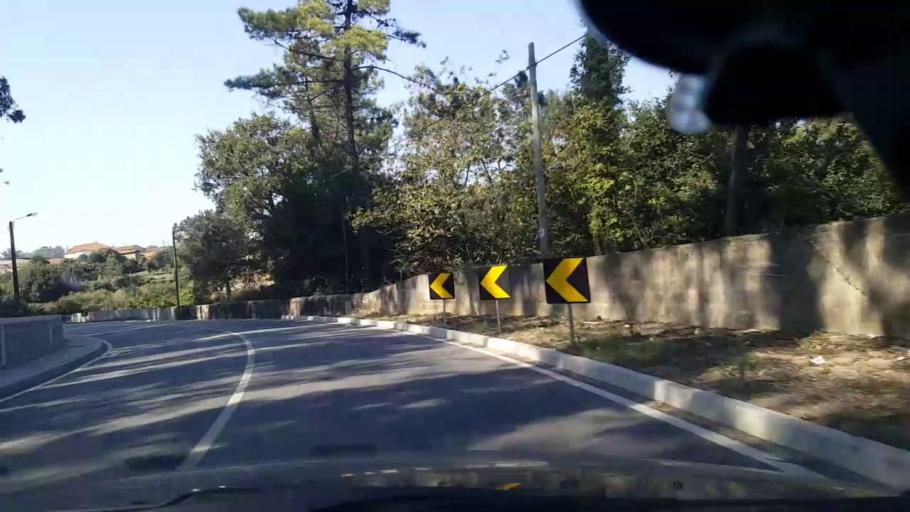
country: PT
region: Porto
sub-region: Vila do Conde
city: Arvore
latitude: 41.3883
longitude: -8.6863
